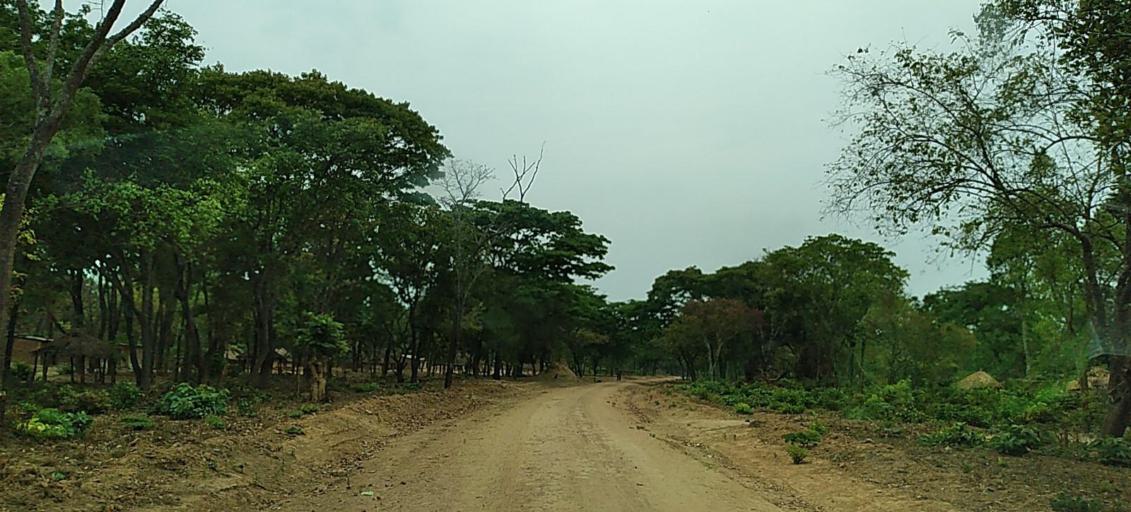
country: ZM
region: North-Western
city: Solwezi
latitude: -12.5443
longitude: 26.5281
